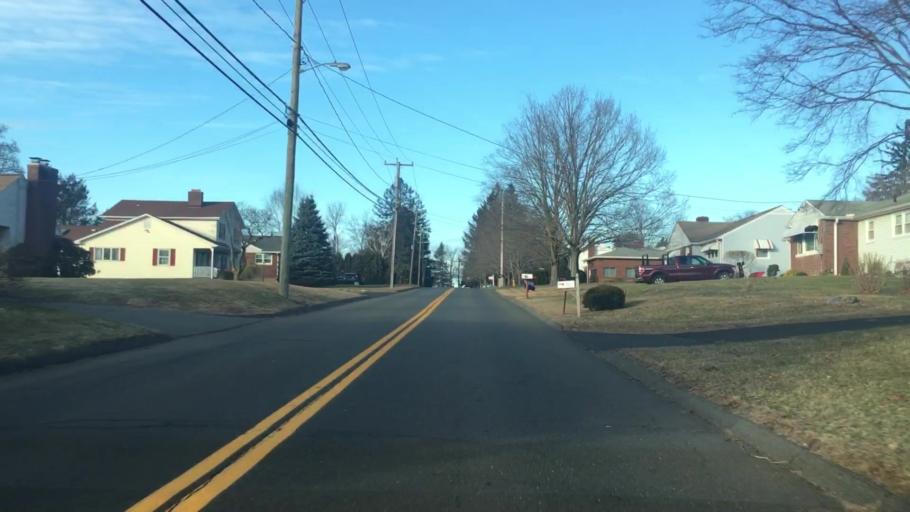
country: US
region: Connecticut
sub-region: Middlesex County
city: Middletown
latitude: 41.5297
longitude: -72.6504
